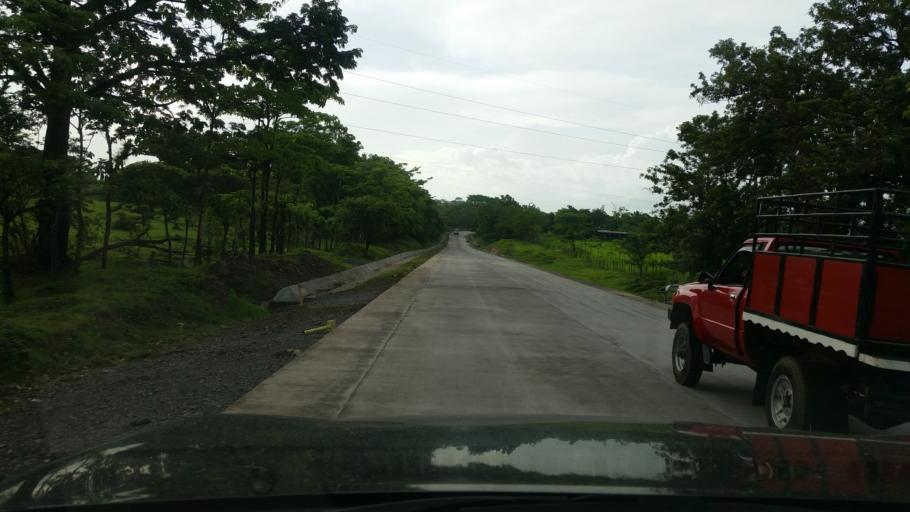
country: NI
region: Matagalpa
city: Rio Blanco
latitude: 13.0978
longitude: -85.0645
